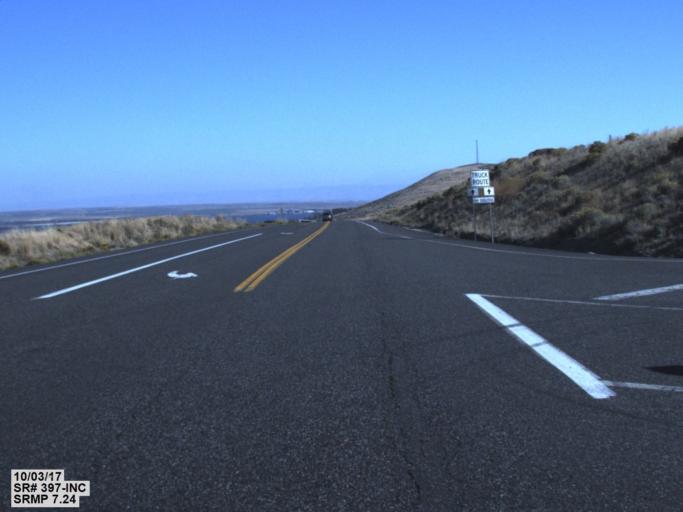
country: US
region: Washington
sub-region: Benton County
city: Finley
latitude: 46.1269
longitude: -119.0666
